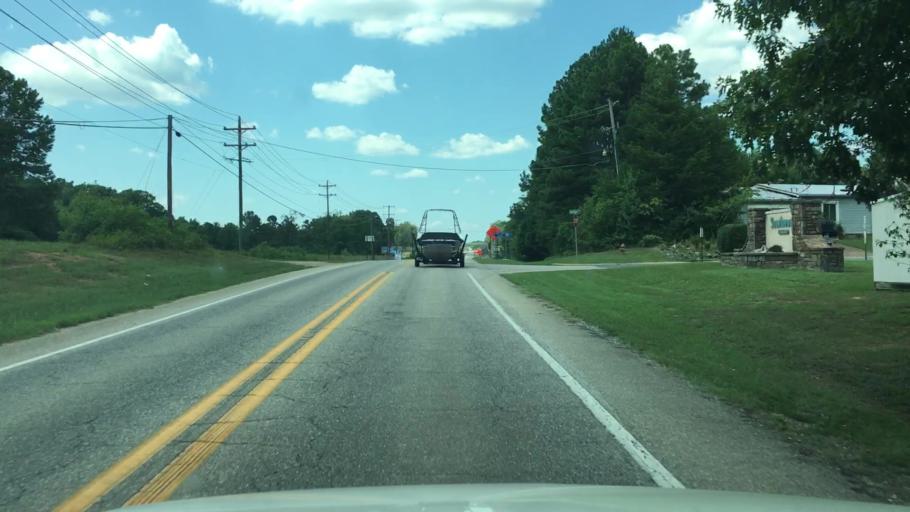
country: US
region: Arkansas
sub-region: Garland County
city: Lake Hamilton
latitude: 34.4100
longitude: -93.0930
